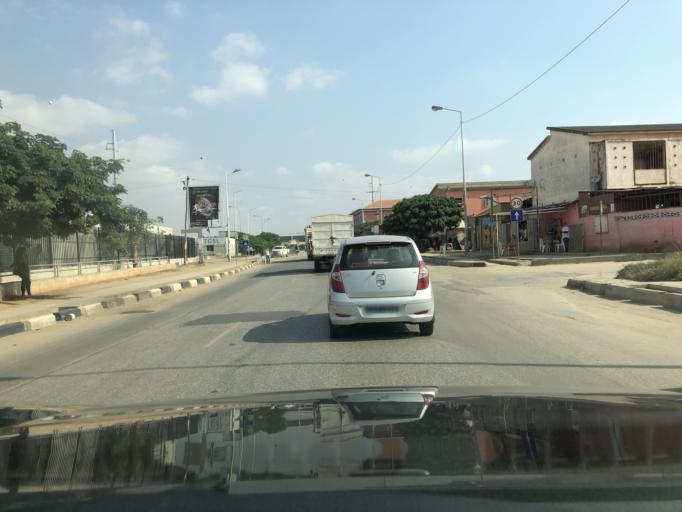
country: AO
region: Luanda
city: Luanda
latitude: -8.8369
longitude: 13.2545
